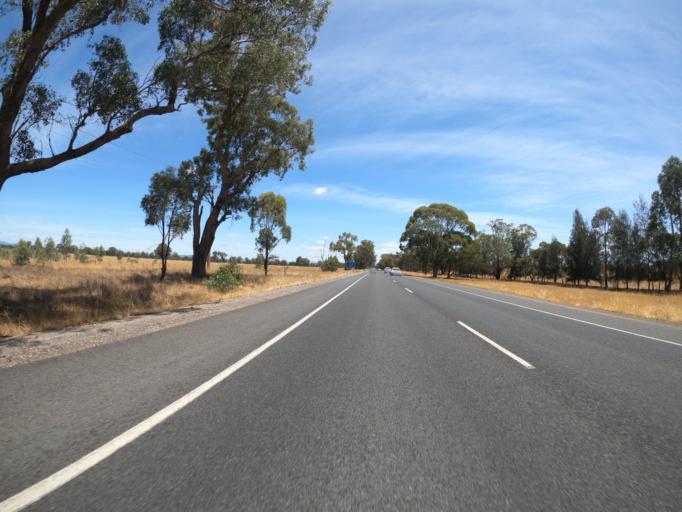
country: AU
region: Victoria
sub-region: Benalla
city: Benalla
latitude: -36.5274
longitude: 146.0477
